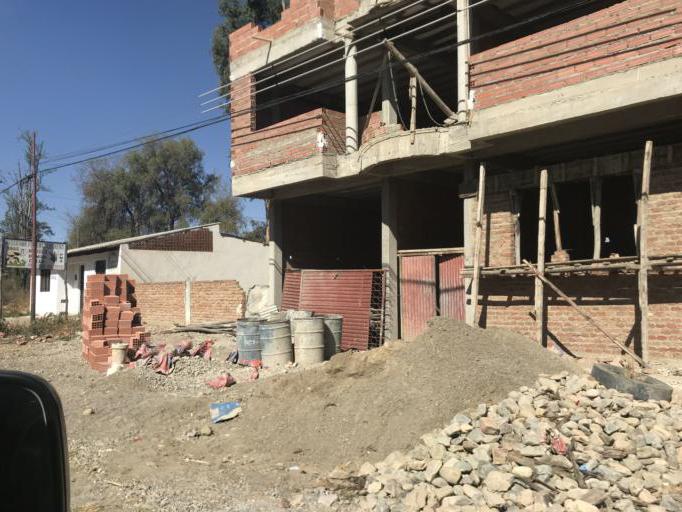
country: BO
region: Cochabamba
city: Punata
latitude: -17.5578
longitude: -65.8643
